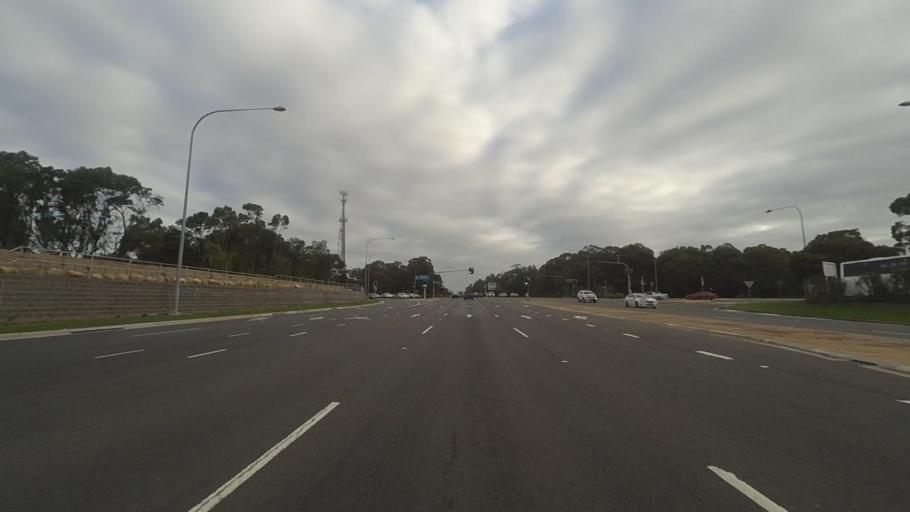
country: AU
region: New South Wales
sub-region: Sutherland Shire
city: Menai
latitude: -34.0121
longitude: 151.0103
